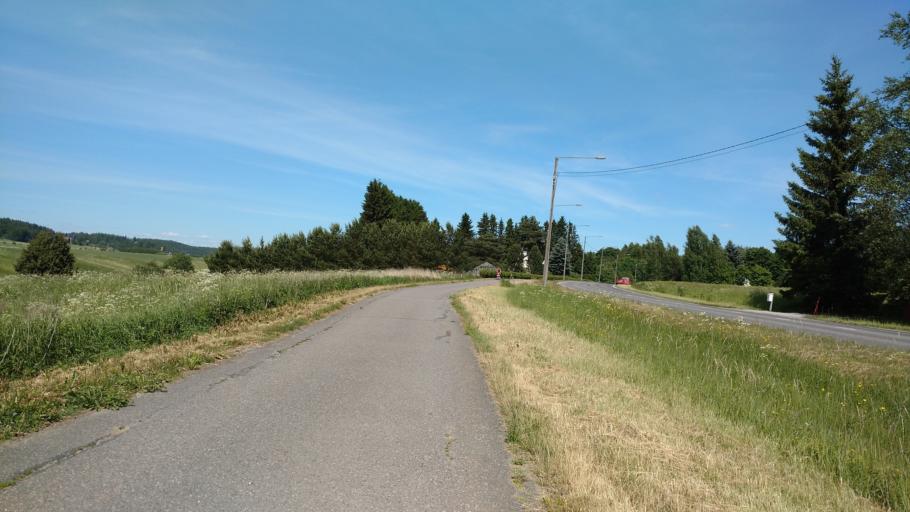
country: FI
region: Varsinais-Suomi
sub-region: Salo
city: Salo
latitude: 60.3999
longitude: 23.1596
